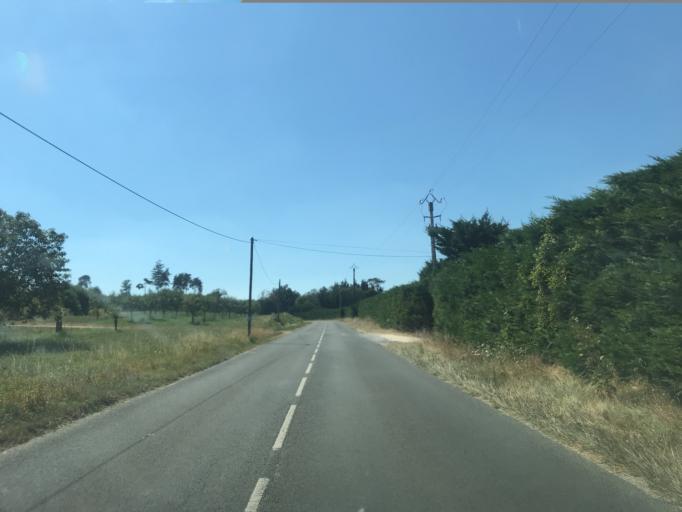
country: FR
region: Aquitaine
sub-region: Departement de la Dordogne
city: Sarlat-la-Caneda
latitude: 44.9607
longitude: 1.2506
